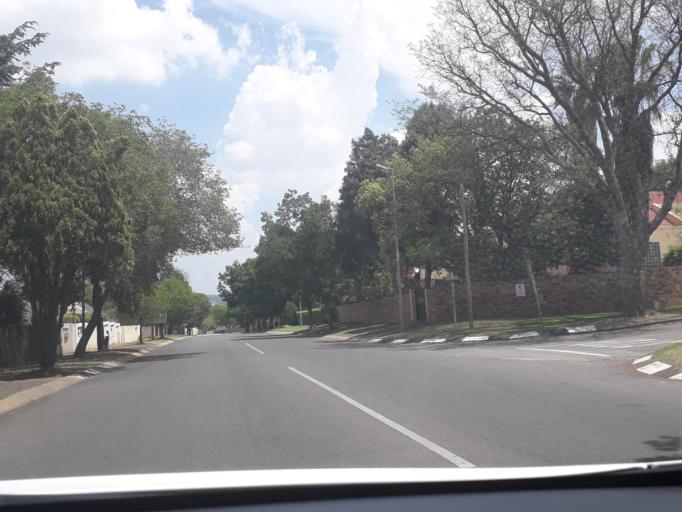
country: ZA
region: Gauteng
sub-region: City of Johannesburg Metropolitan Municipality
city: Midrand
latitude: -26.0395
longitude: 28.0735
